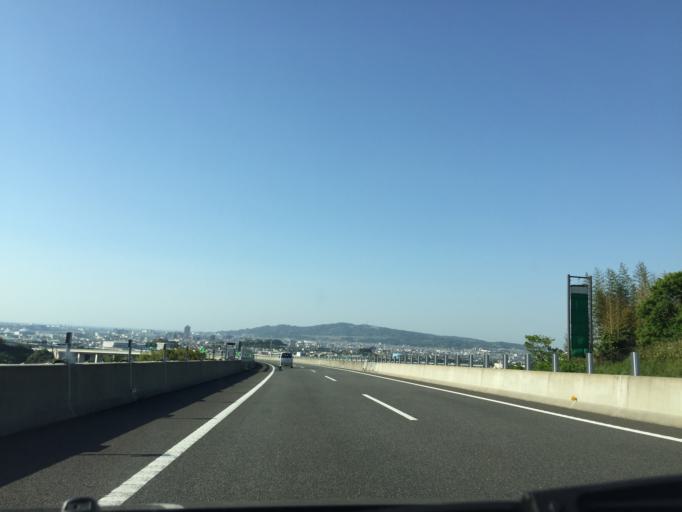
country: JP
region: Shizuoka
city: Shizuoka-shi
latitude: 35.0595
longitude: 138.4812
